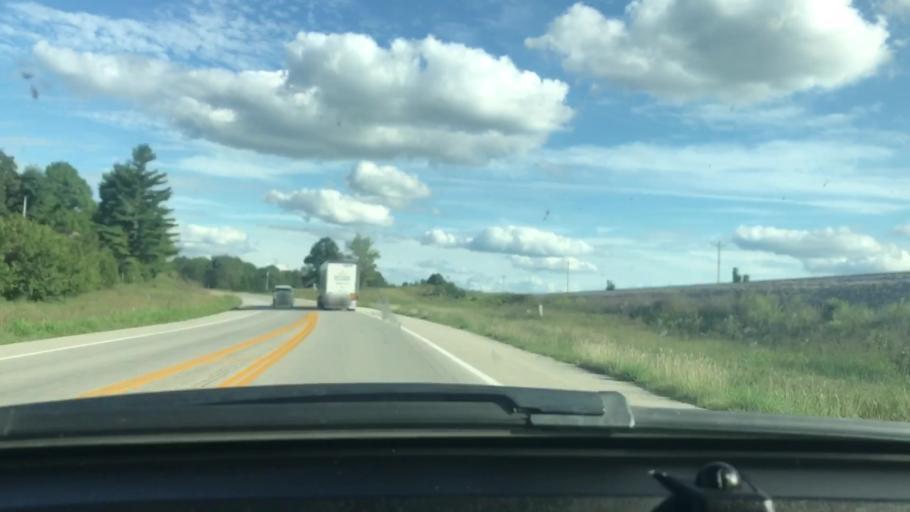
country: US
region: Missouri
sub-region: Oregon County
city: Thayer
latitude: 36.5910
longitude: -91.6426
